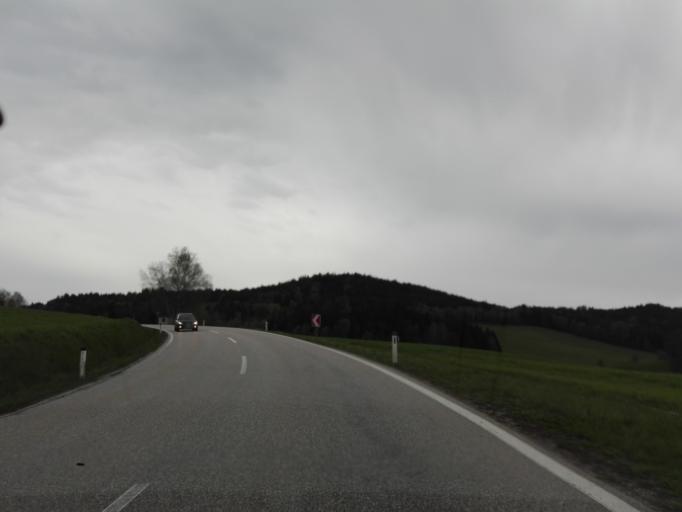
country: AT
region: Upper Austria
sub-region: Politischer Bezirk Rohrbach
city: Schlaegl
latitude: 48.6179
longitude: 13.9694
